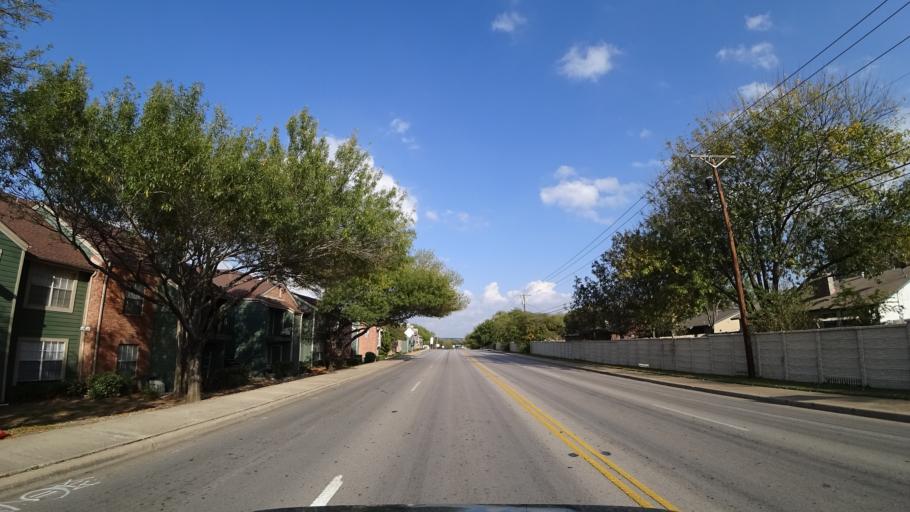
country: US
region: Texas
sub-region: Williamson County
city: Round Rock
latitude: 30.4950
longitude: -97.6708
